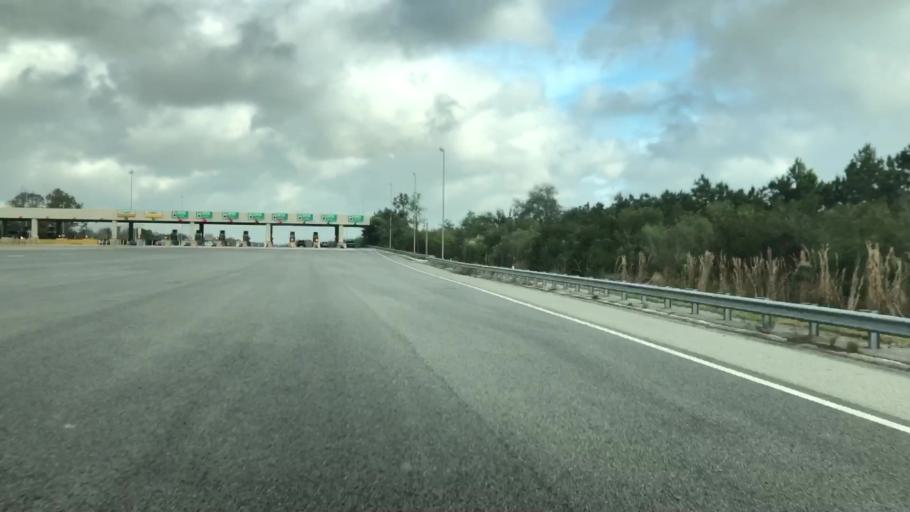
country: US
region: Florida
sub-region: Osceola County
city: Saint Cloud
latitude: 28.1800
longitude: -81.3027
